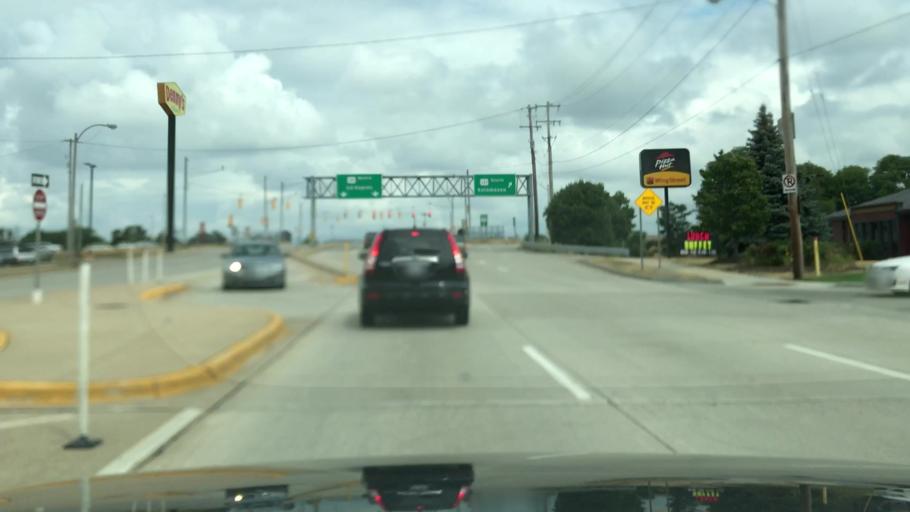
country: US
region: Michigan
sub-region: Kent County
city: Wyoming
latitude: 42.8841
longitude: -85.6829
